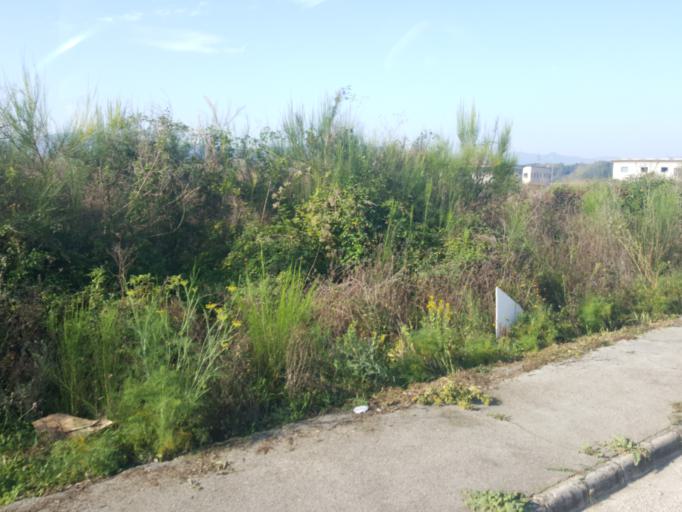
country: IT
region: Latium
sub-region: Citta metropolitana di Roma Capitale
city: Colleferro
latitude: 41.7572
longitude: 12.9923
